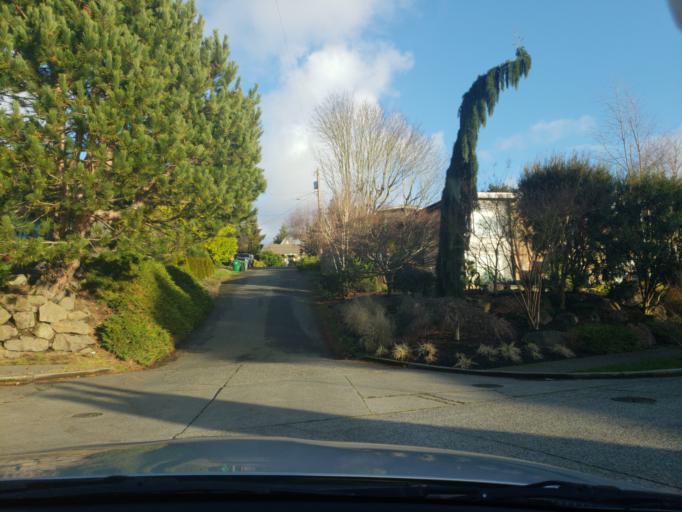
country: US
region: Washington
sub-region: King County
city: Seattle
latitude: 47.6377
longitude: -122.3969
